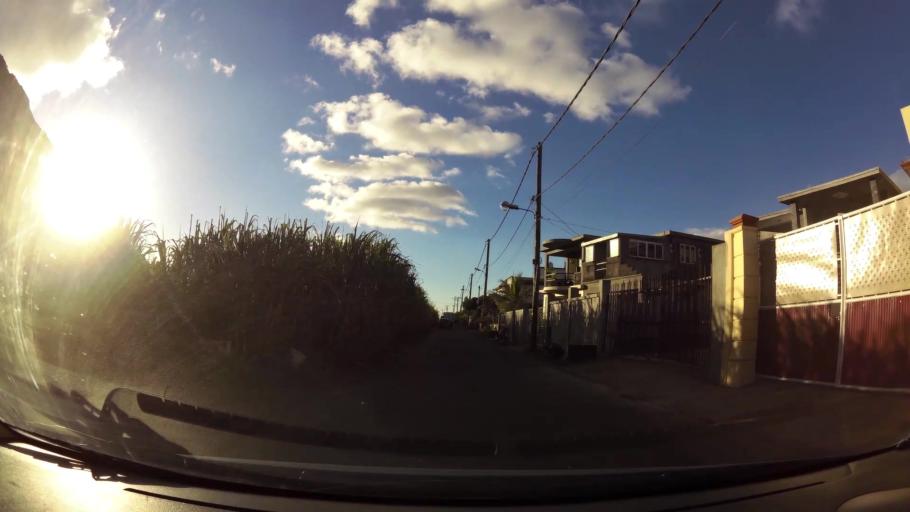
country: MU
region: Plaines Wilhems
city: Quatre Bornes
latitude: -20.2621
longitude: 57.4623
